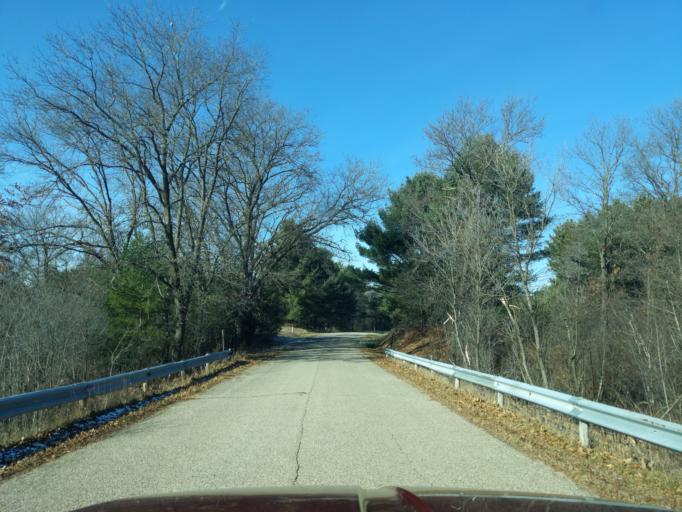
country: US
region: Wisconsin
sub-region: Waushara County
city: Silver Lake
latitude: 44.1118
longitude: -89.1708
